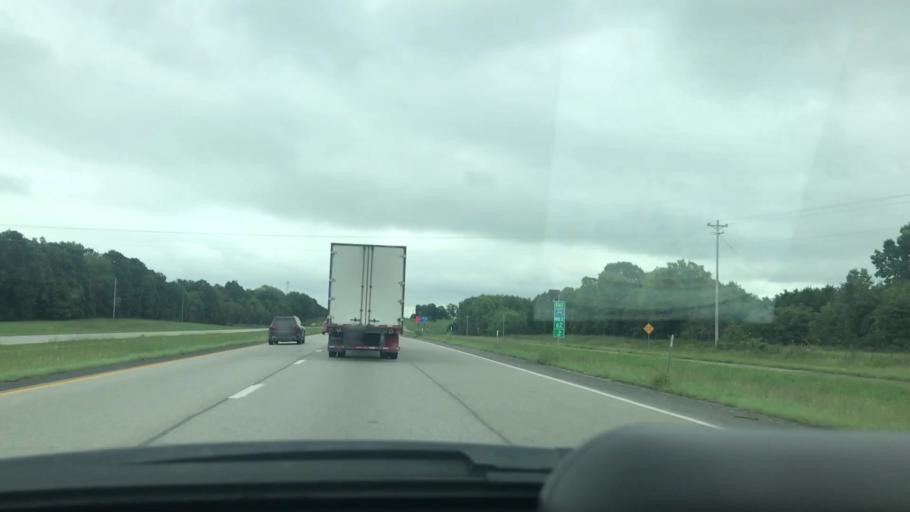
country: US
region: Missouri
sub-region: Greene County
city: Republic
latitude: 37.1858
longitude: -93.5658
